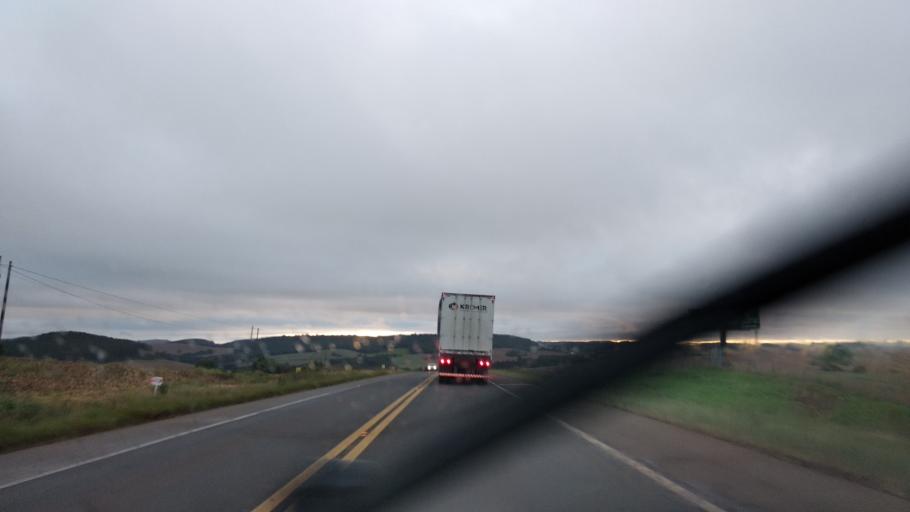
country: BR
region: Santa Catarina
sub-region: Campos Novos
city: Campos Novos
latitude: -27.3753
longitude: -51.0757
